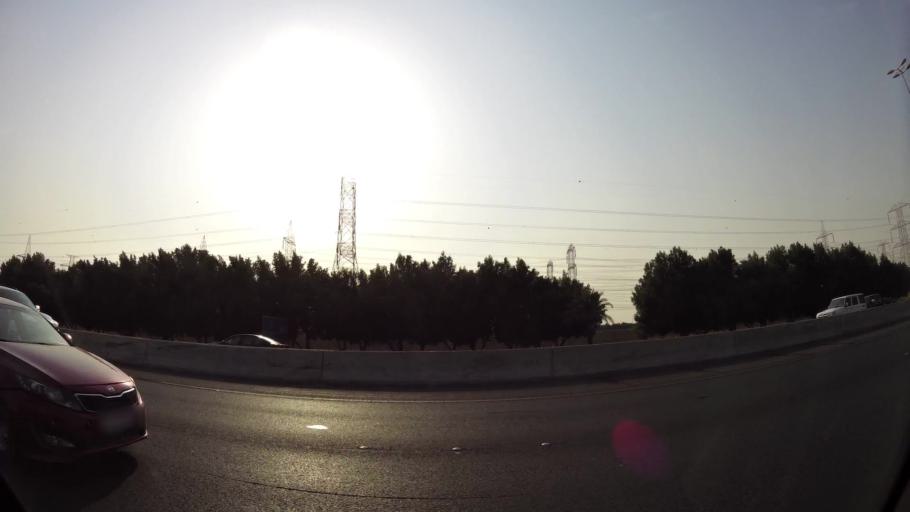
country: KW
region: Mubarak al Kabir
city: Sabah as Salim
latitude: 29.2440
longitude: 48.0488
